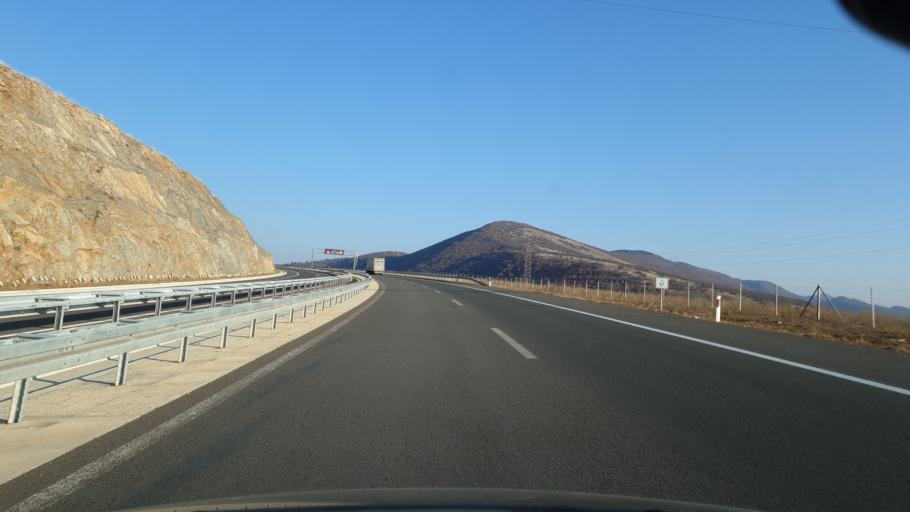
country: RS
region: Central Serbia
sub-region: Pirotski Okrug
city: Dimitrovgrad
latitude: 43.0155
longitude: 22.7528
